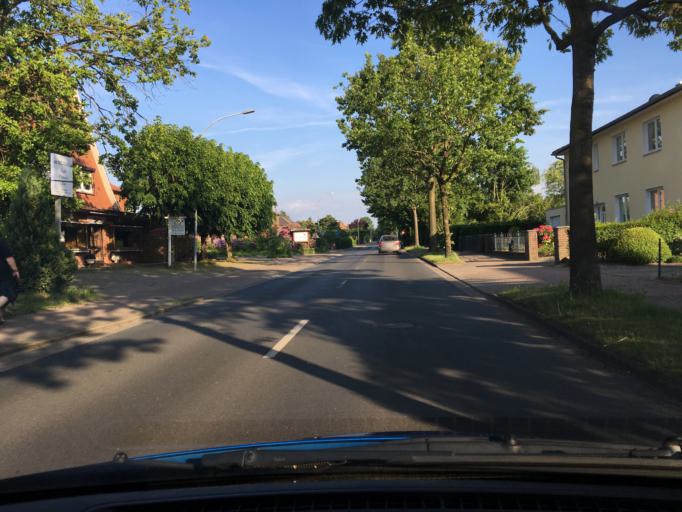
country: DE
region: Lower Saxony
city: Tostedt
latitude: 53.2674
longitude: 9.7283
